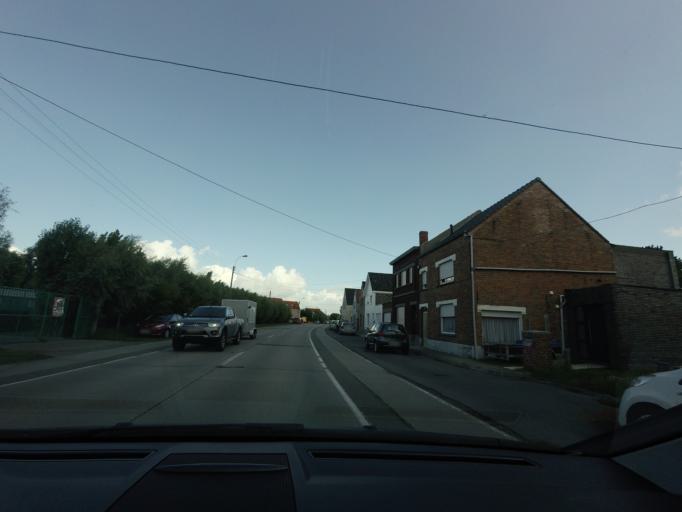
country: BE
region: Flanders
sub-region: Provincie West-Vlaanderen
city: De Haan
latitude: 51.2539
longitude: 3.0092
